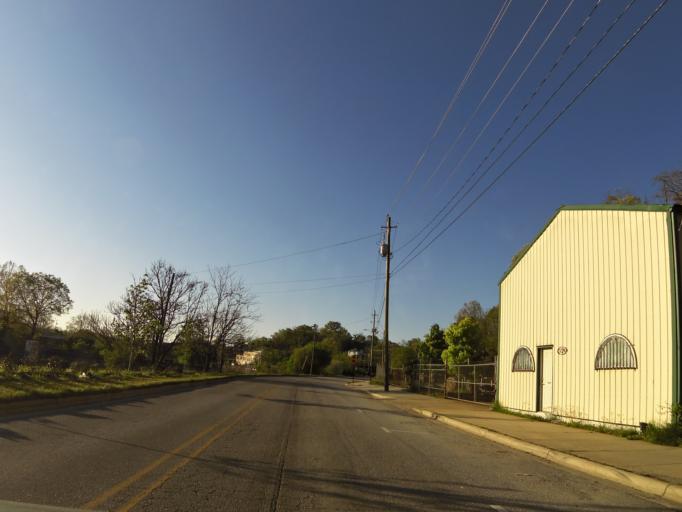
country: US
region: North Carolina
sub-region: Buncombe County
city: Asheville
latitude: 35.5826
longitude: -82.5647
